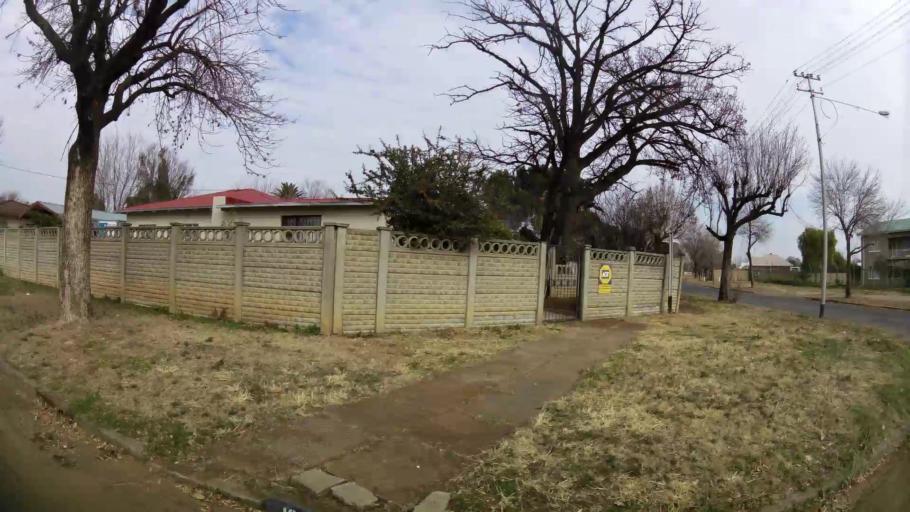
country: ZA
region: Orange Free State
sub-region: Mangaung Metropolitan Municipality
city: Bloemfontein
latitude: -29.1292
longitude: 26.1993
